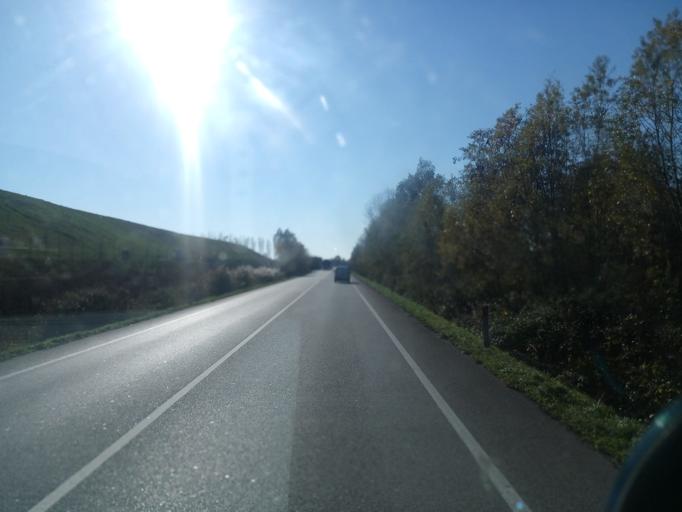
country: IT
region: Veneto
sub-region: Provincia di Padova
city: Campodarsego
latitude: 45.4913
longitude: 11.9257
